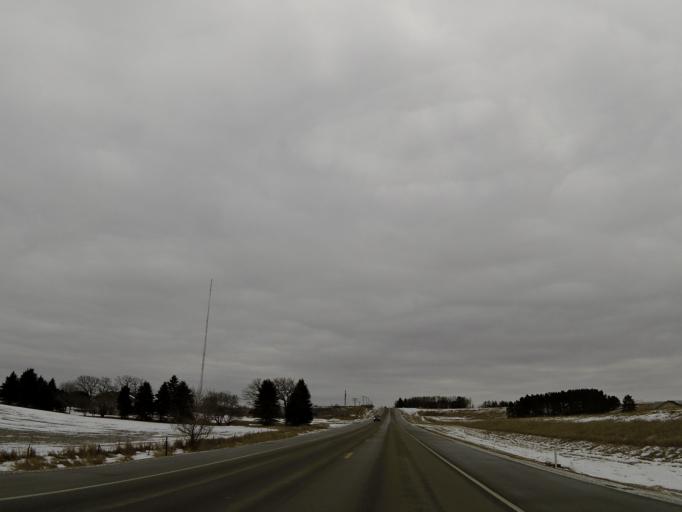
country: US
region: Minnesota
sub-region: Washington County
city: Cottage Grove
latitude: 44.8708
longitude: -92.9032
